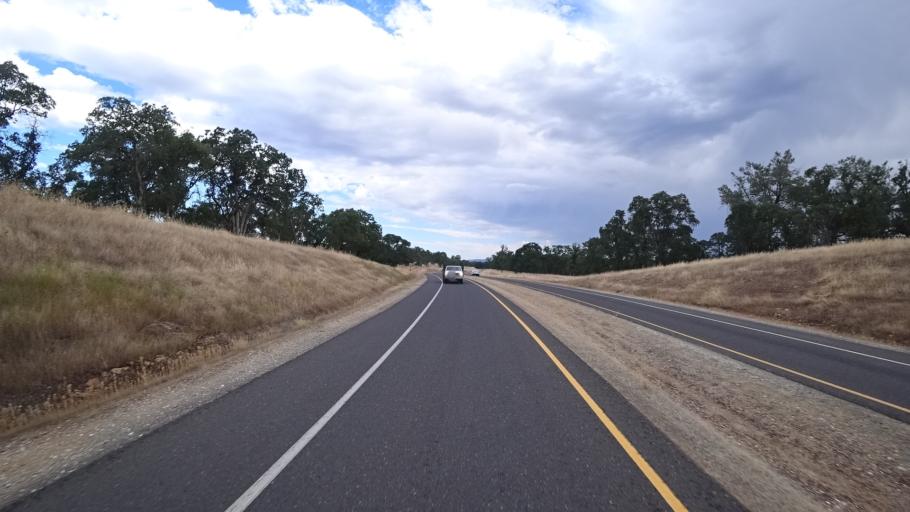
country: US
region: California
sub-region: Calaveras County
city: Copperopolis
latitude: 37.9454
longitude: -120.6504
